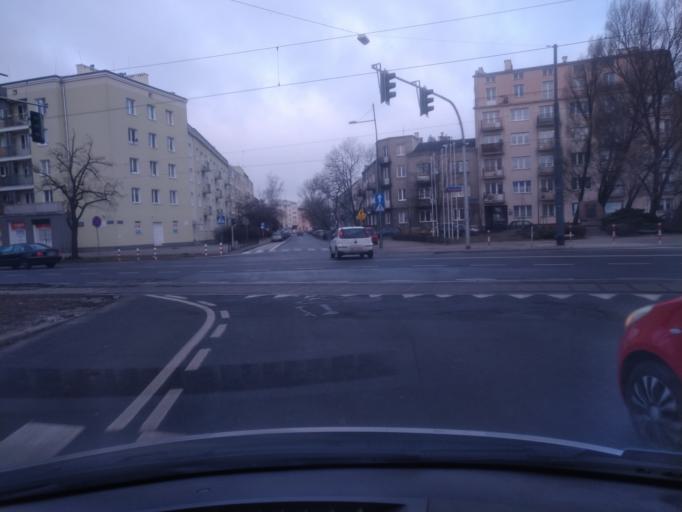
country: PL
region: Masovian Voivodeship
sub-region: Warszawa
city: Praga Poludnie
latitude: 52.2433
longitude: 21.0779
